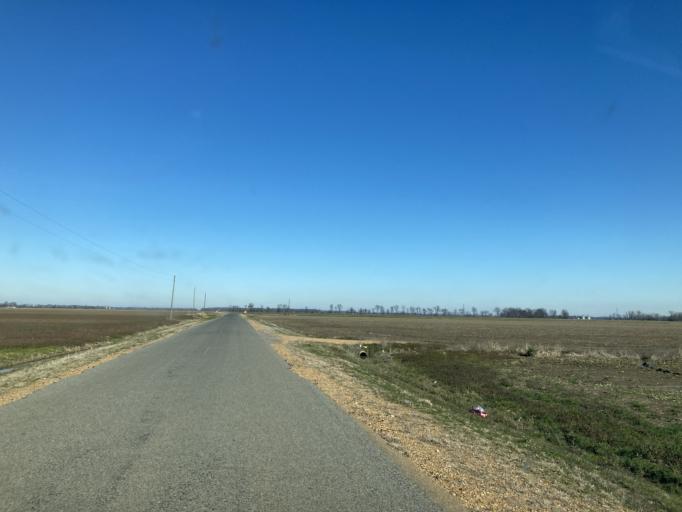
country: US
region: Mississippi
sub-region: Yazoo County
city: Yazoo City
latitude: 32.9743
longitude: -90.6052
